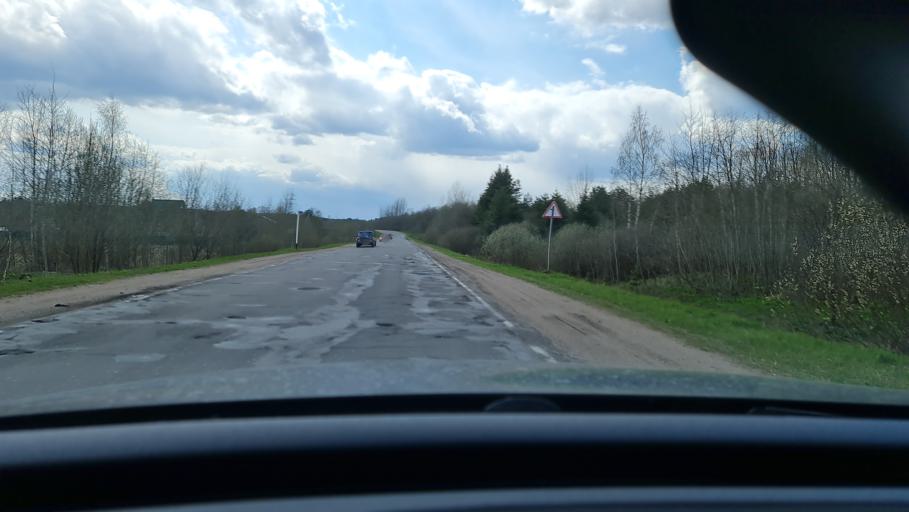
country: RU
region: Tverskaya
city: Toropets
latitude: 56.4316
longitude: 31.6458
